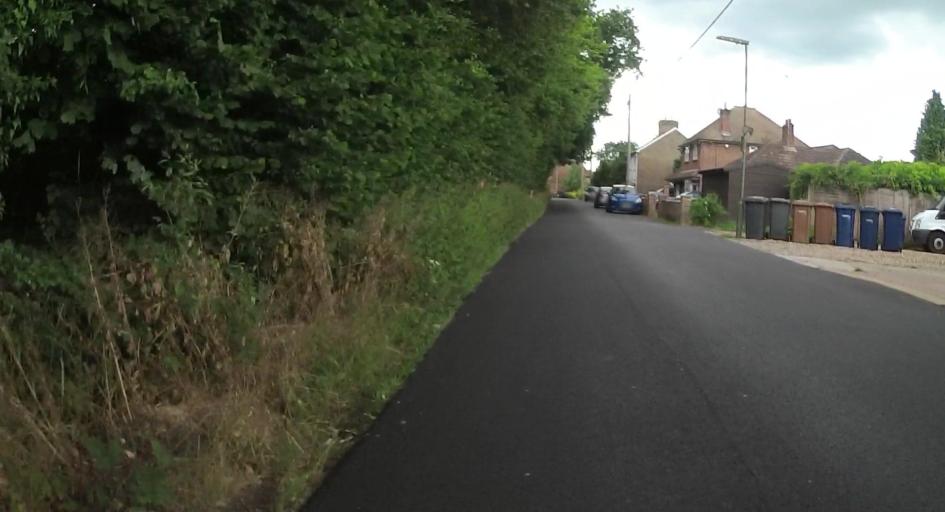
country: GB
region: England
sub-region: Hampshire
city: Aldershot
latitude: 51.2319
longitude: -0.7602
